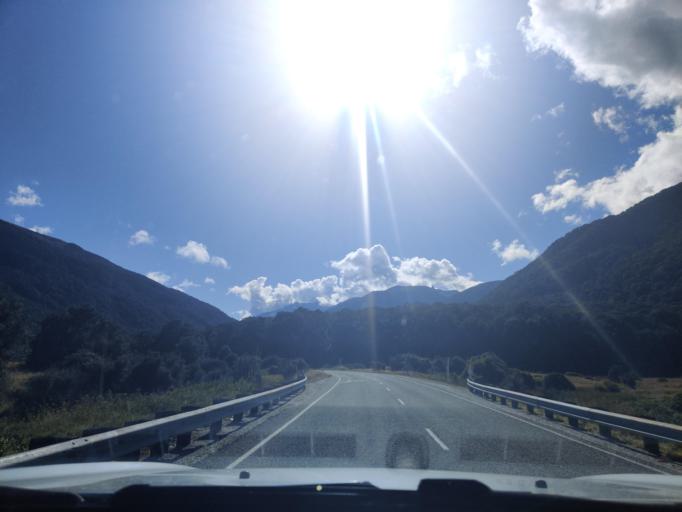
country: NZ
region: Otago
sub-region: Queenstown-Lakes District
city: Wanaka
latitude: -44.1562
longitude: 169.3000
